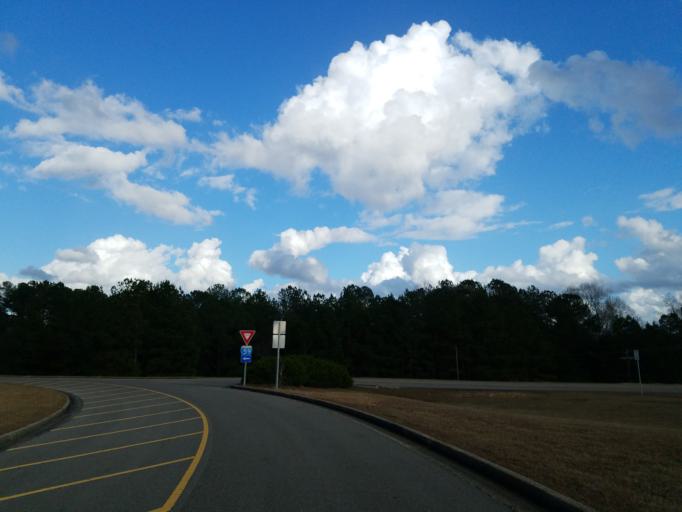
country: US
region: Mississippi
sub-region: Forrest County
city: Rawls Springs
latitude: 31.4659
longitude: -89.3326
